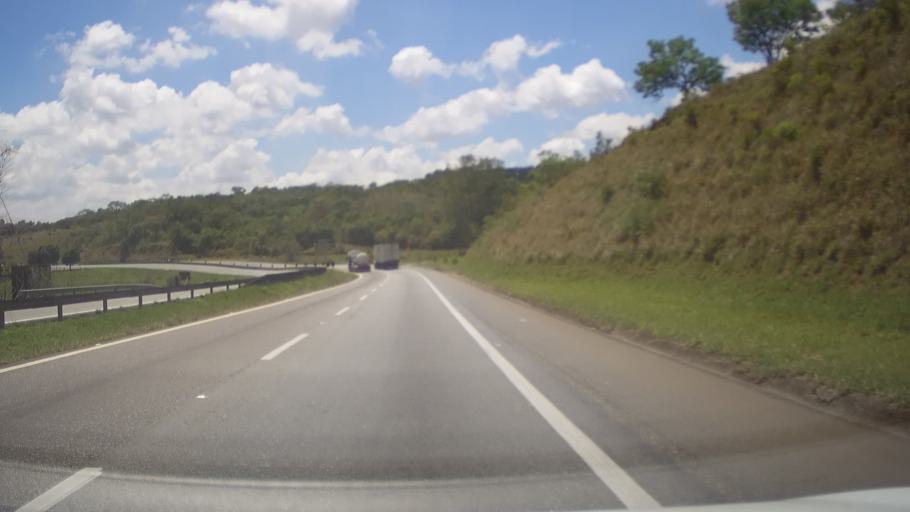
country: BR
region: Minas Gerais
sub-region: Campanha
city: Campanha
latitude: -21.8330
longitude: -45.5012
